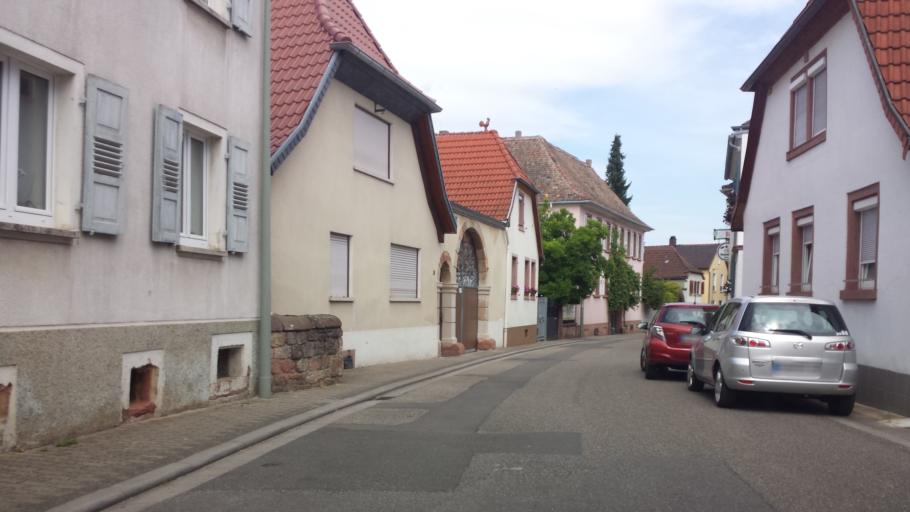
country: DE
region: Rheinland-Pfalz
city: Edesheim
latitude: 49.2625
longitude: 8.1312
